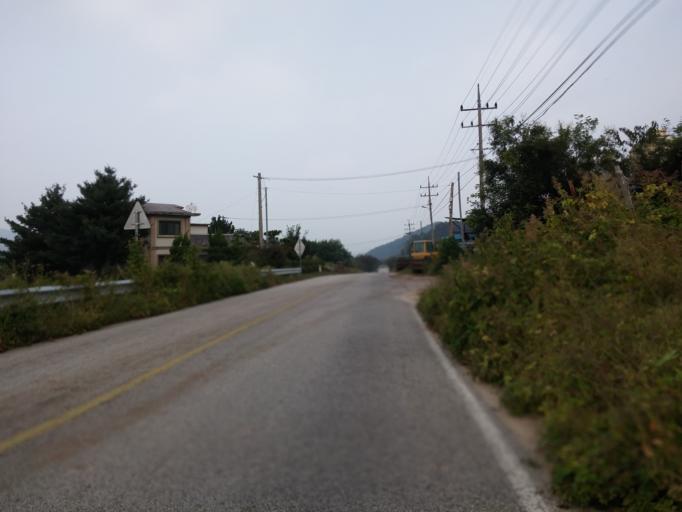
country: KR
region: Chungcheongbuk-do
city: Okcheon
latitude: 36.4128
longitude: 127.7650
